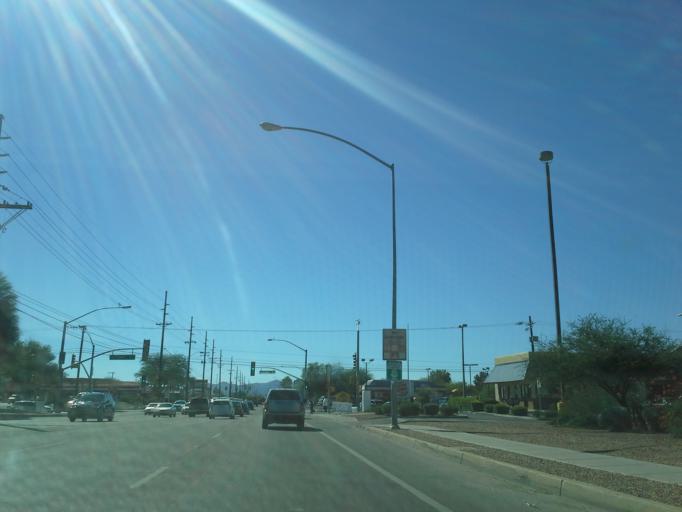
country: US
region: Arizona
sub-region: Pima County
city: Tucson
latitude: 32.2507
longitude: -110.9088
